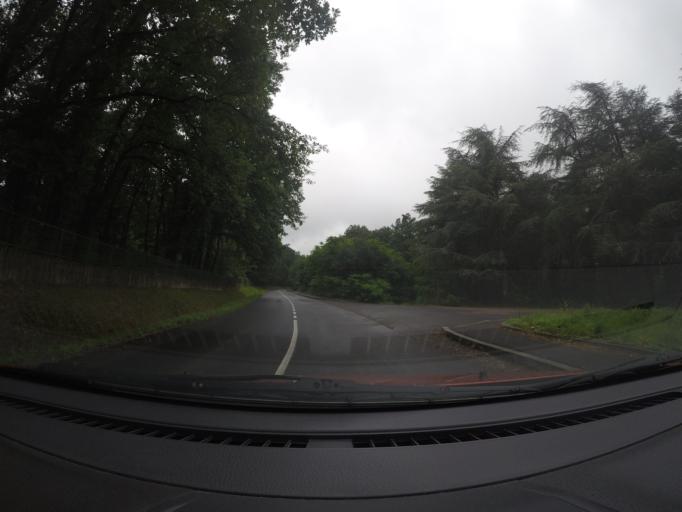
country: RS
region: Central Serbia
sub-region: Belgrade
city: Zvezdara
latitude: 44.6835
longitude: 20.5421
